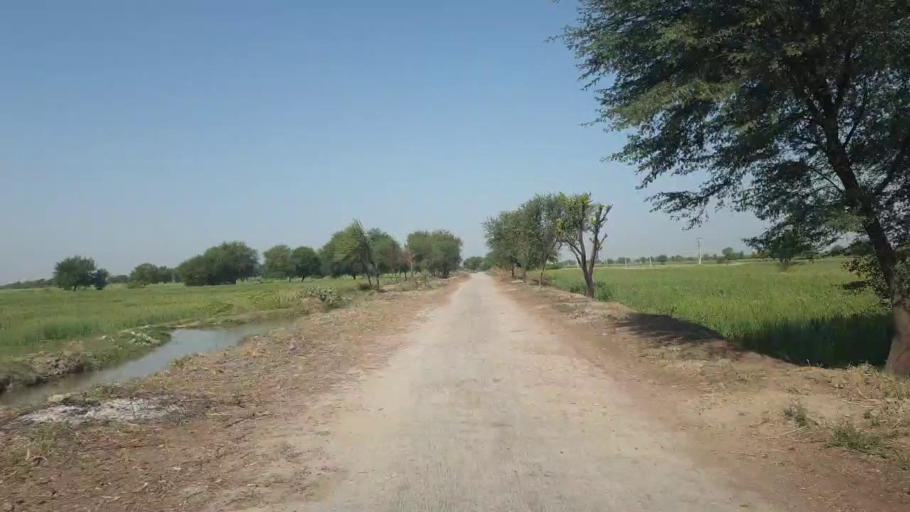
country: PK
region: Sindh
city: Umarkot
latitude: 25.2970
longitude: 69.6262
